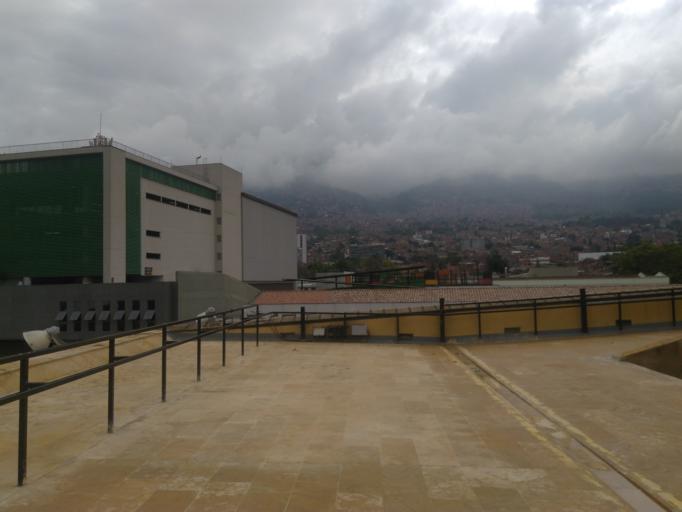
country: CO
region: Antioquia
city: Medellin
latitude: 6.2682
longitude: -75.5661
